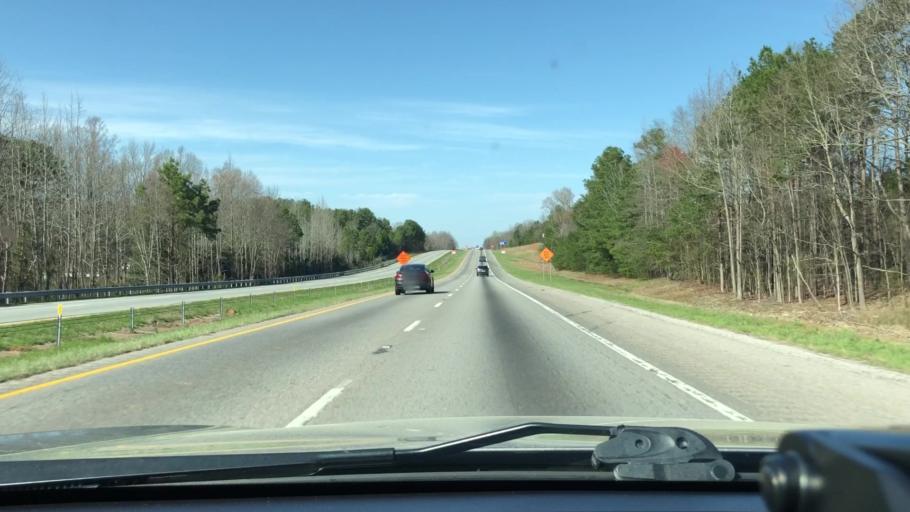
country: US
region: South Carolina
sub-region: Spartanburg County
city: Roebuck
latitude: 34.8987
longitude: -81.9920
